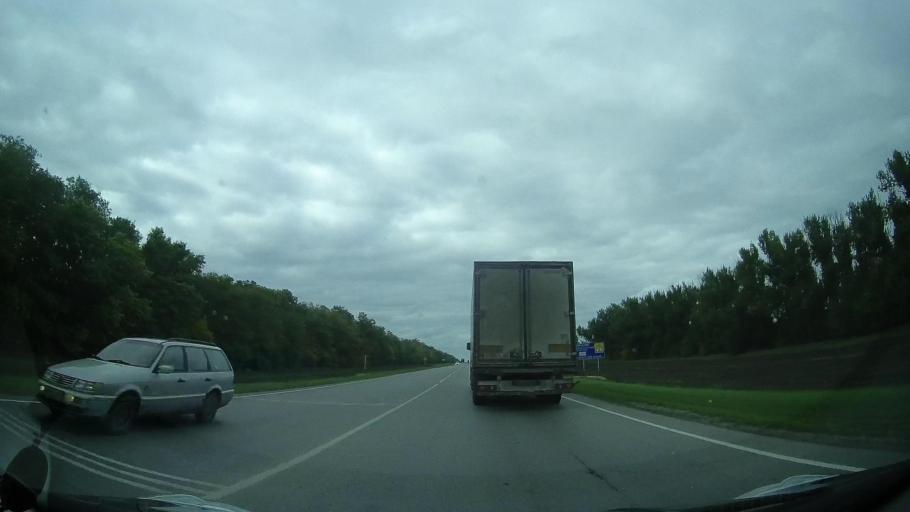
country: RU
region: Rostov
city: Yegorlykskaya
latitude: 46.6266
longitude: 40.5918
